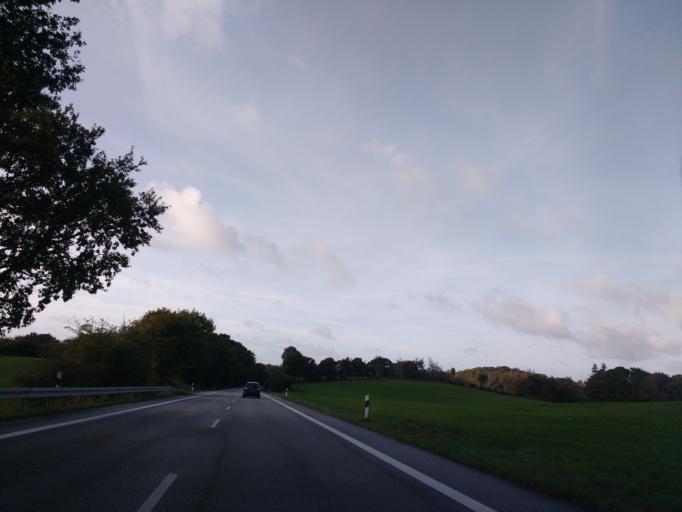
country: DE
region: Schleswig-Holstein
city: Schashagen
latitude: 54.1280
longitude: 10.8939
